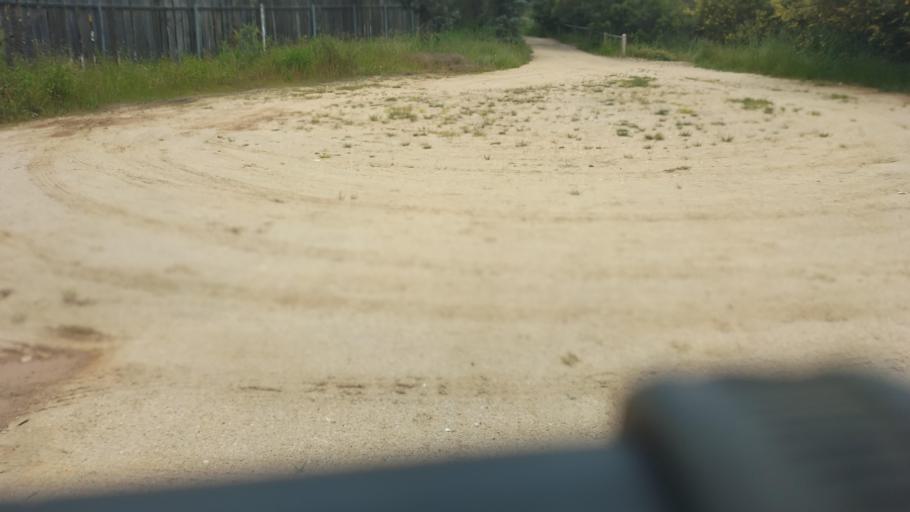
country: AU
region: Victoria
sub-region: Mount Alexander
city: Castlemaine
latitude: -37.0744
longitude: 144.2028
